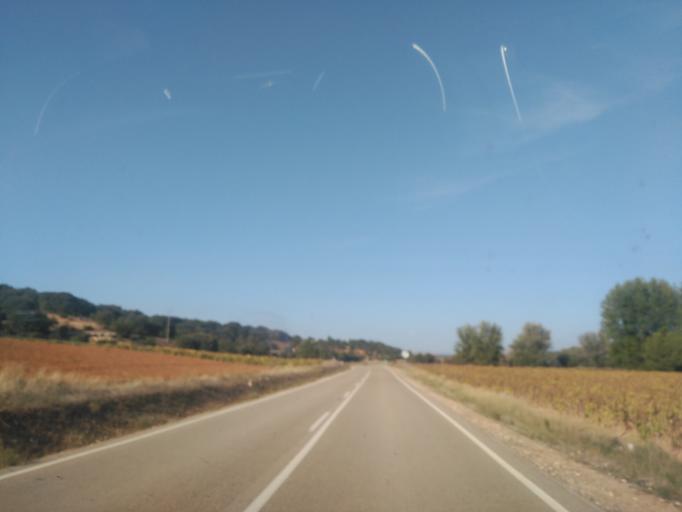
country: ES
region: Castille and Leon
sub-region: Provincia de Soria
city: Alcubilla de Avellaneda
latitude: 41.7365
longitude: -3.2950
